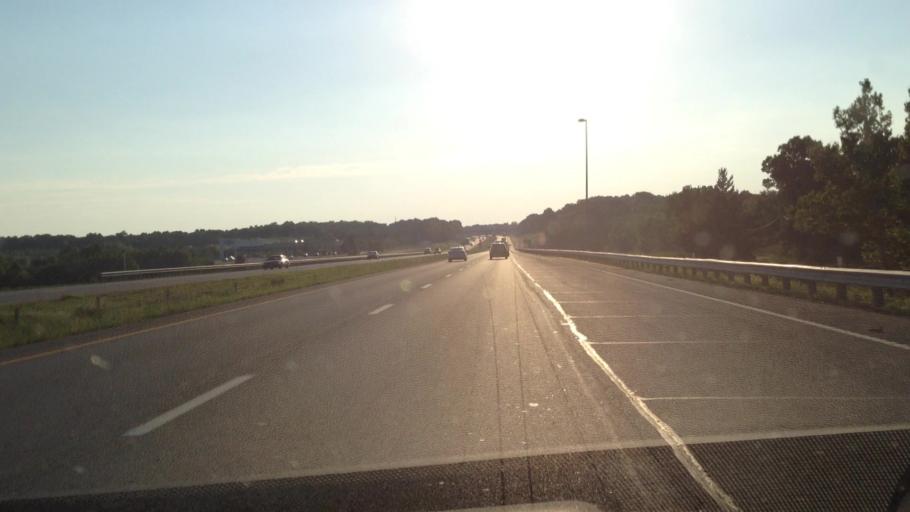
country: US
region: Missouri
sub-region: Jasper County
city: Duquesne
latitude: 37.0464
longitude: -94.4840
